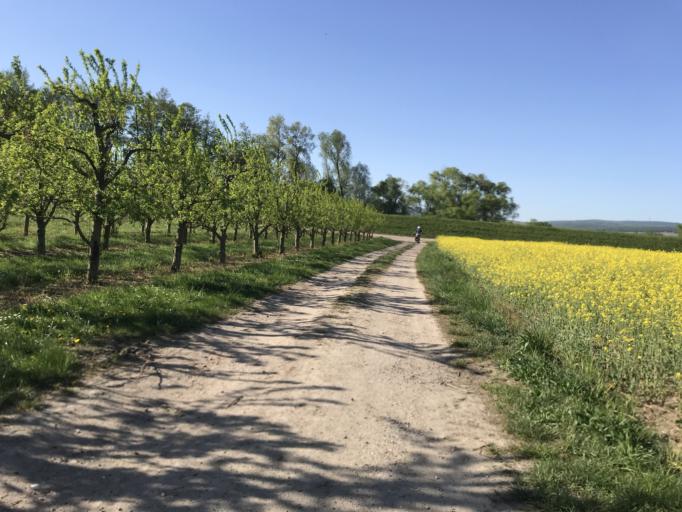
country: DE
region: Hesse
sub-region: Regierungsbezirk Darmstadt
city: Eltville
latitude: 50.0093
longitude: 8.1251
